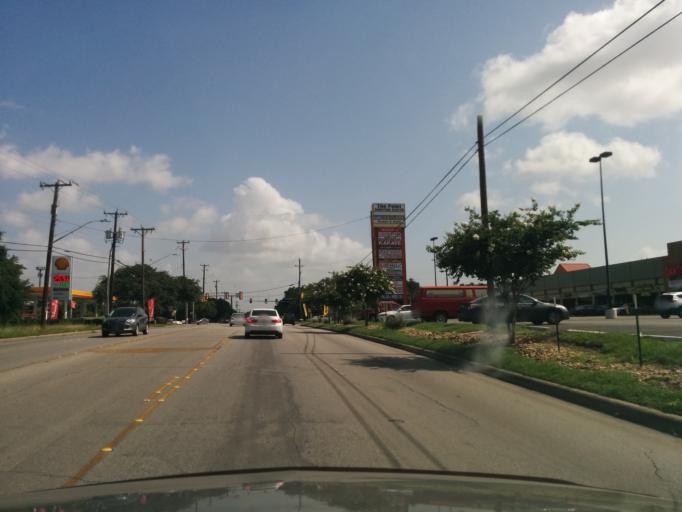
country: US
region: Texas
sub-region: Bexar County
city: Leon Valley
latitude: 29.5558
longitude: -98.6149
